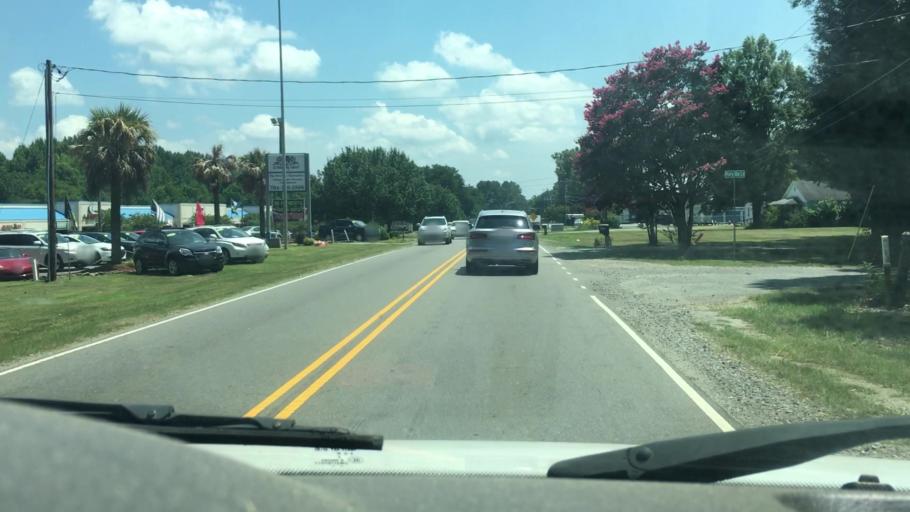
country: US
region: North Carolina
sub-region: Iredell County
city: Mooresville
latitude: 35.5827
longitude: -80.8399
